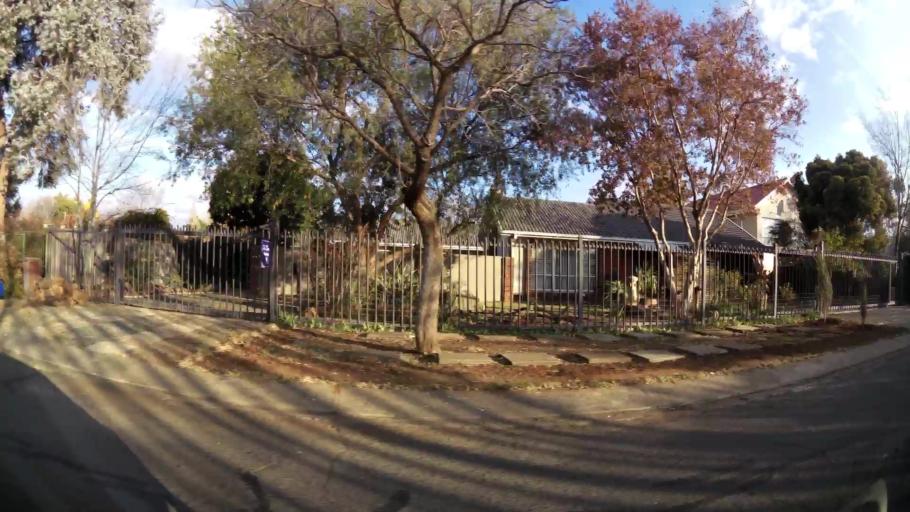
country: ZA
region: Orange Free State
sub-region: Mangaung Metropolitan Municipality
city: Bloemfontein
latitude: -29.1461
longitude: 26.1817
